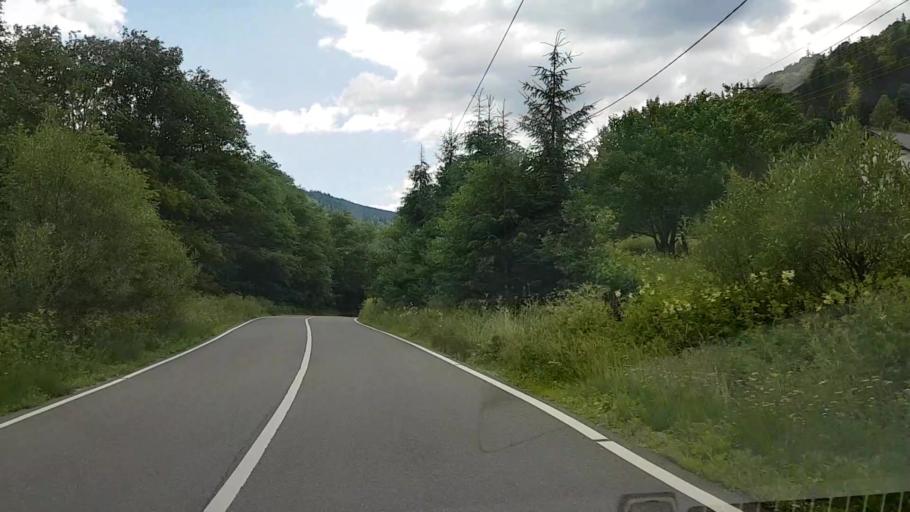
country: RO
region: Suceava
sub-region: Comuna Crucea
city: Crucea
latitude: 47.3284
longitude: 25.6203
